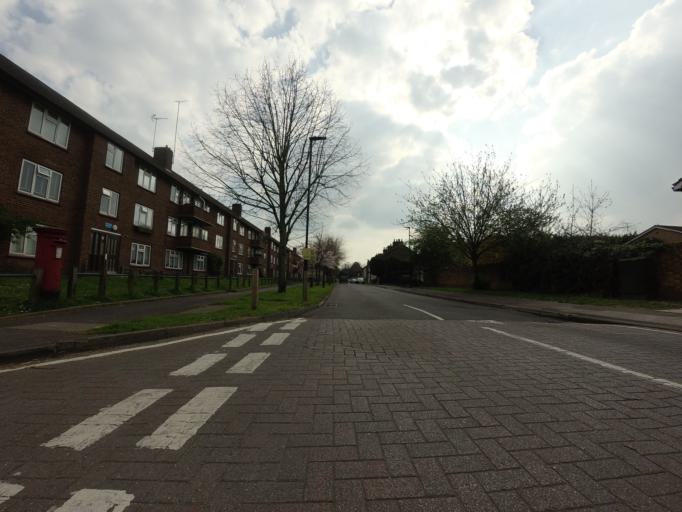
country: GB
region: England
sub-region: Greater London
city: Orpington
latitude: 51.3974
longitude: 0.1158
